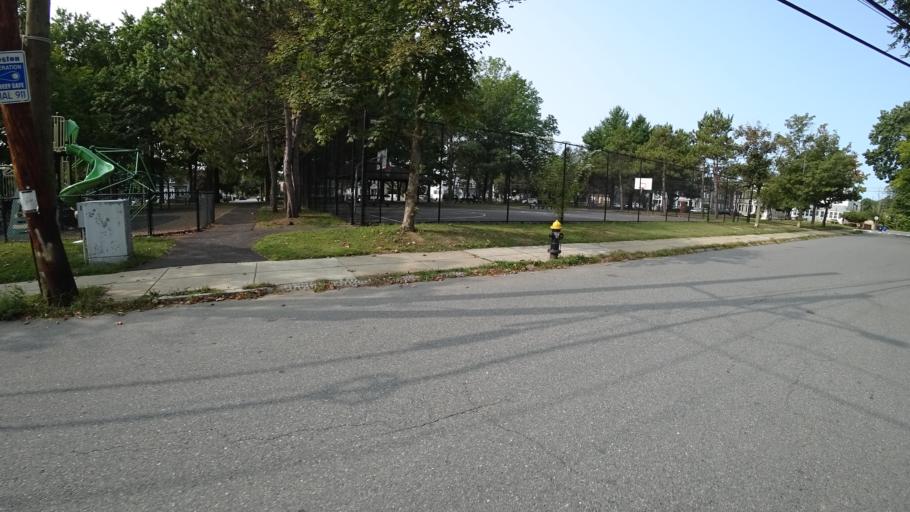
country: US
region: Massachusetts
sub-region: Norfolk County
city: Dedham
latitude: 42.2352
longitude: -71.1318
